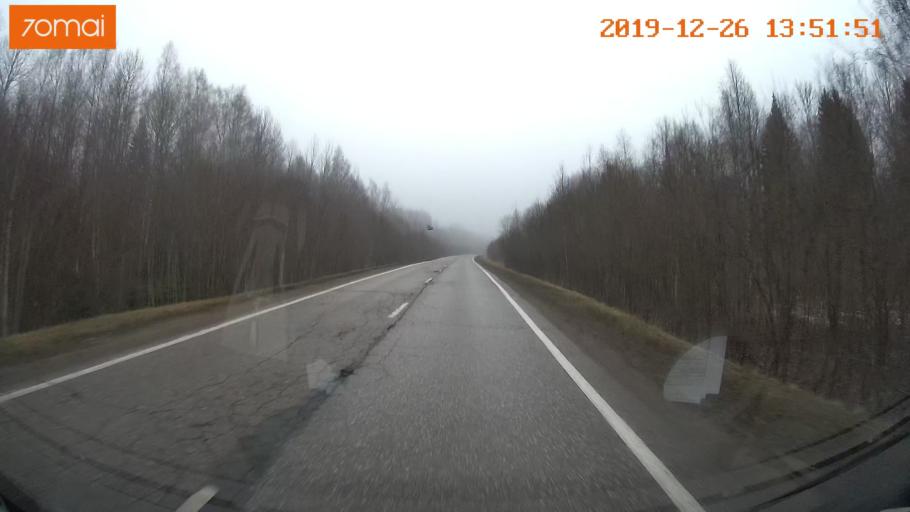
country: RU
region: Jaroslavl
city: Poshekhon'ye
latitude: 58.6391
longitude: 38.5956
